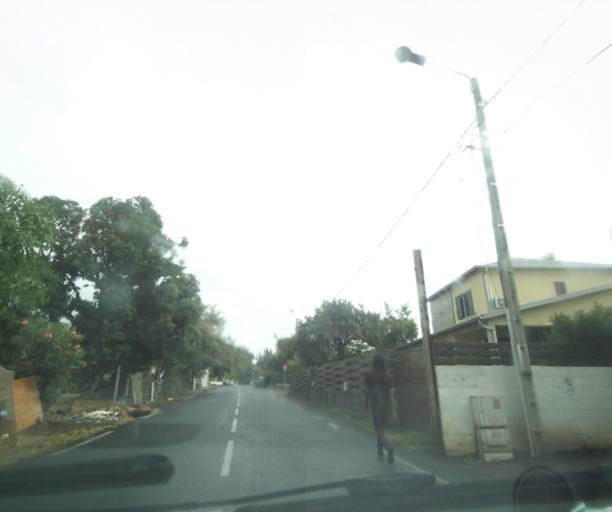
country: RE
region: Reunion
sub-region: Reunion
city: Saint-Paul
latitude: -20.9907
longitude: 55.2849
